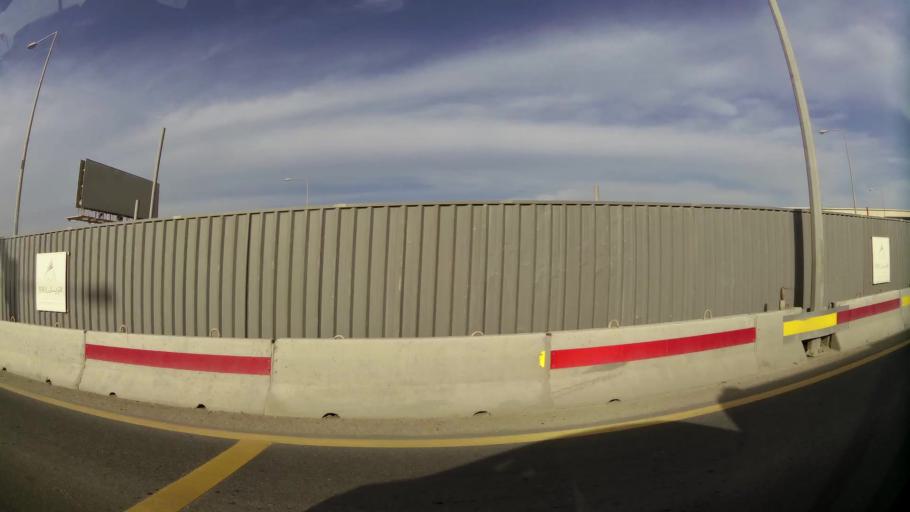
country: QA
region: Al Wakrah
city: Al Wakrah
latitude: 25.1959
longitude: 51.5937
